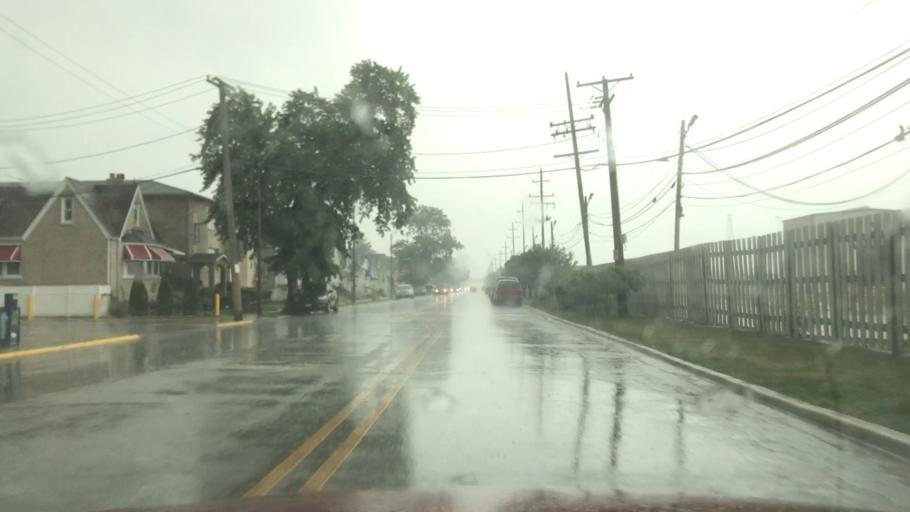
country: US
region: Illinois
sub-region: Cook County
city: Cicero
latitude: 41.8437
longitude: -87.7637
